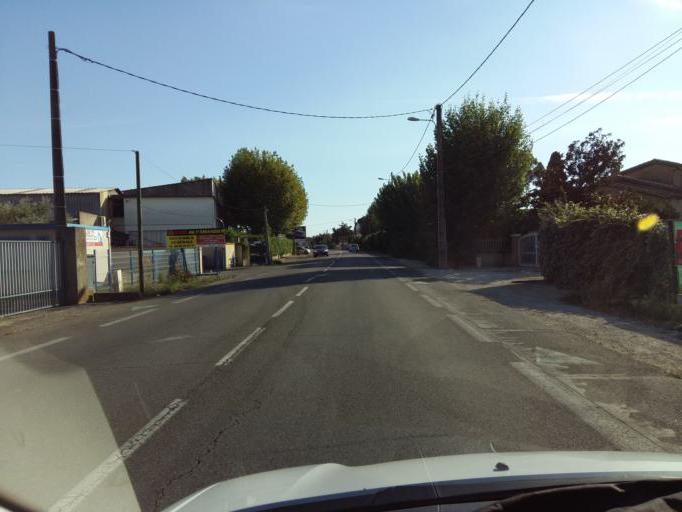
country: FR
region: Provence-Alpes-Cote d'Azur
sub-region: Departement du Vaucluse
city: Le Pontet
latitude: 43.9433
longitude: 4.8531
